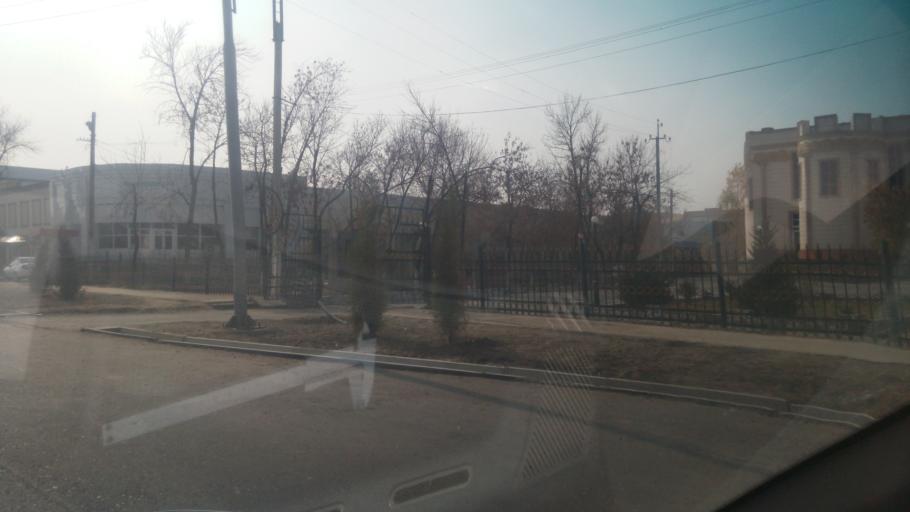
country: UZ
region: Sirdaryo
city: Guliston
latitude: 40.5072
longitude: 68.7737
